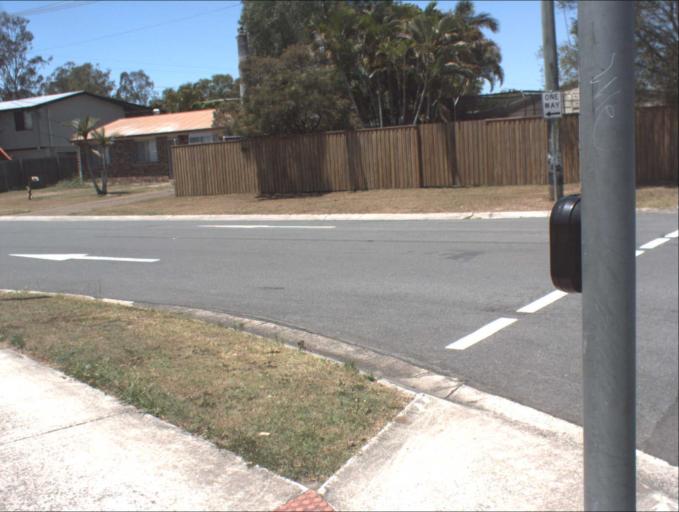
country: AU
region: Queensland
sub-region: Logan
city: Beenleigh
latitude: -27.6857
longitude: 153.1794
